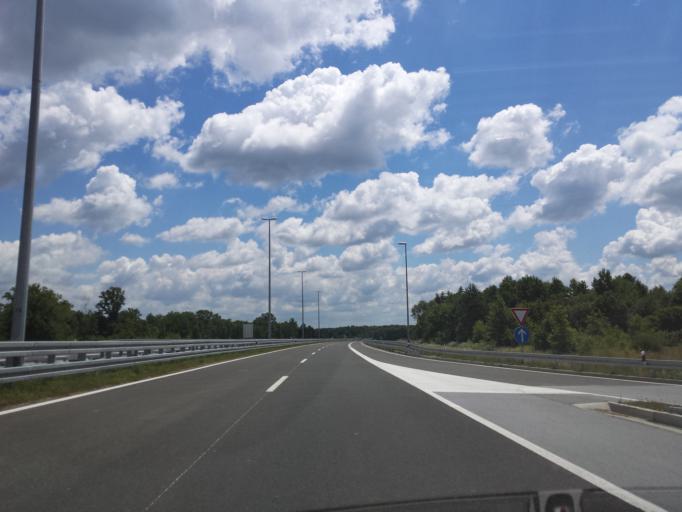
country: HR
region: Sisacko-Moslavacka
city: Lekenik
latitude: 45.5913
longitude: 16.1629
